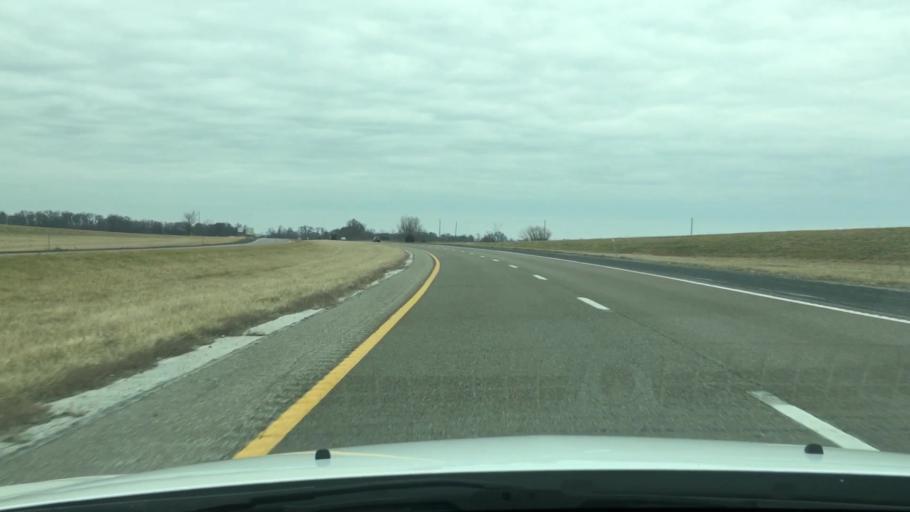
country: US
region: Missouri
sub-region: Audrain County
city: Mexico
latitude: 39.0184
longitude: -91.8861
